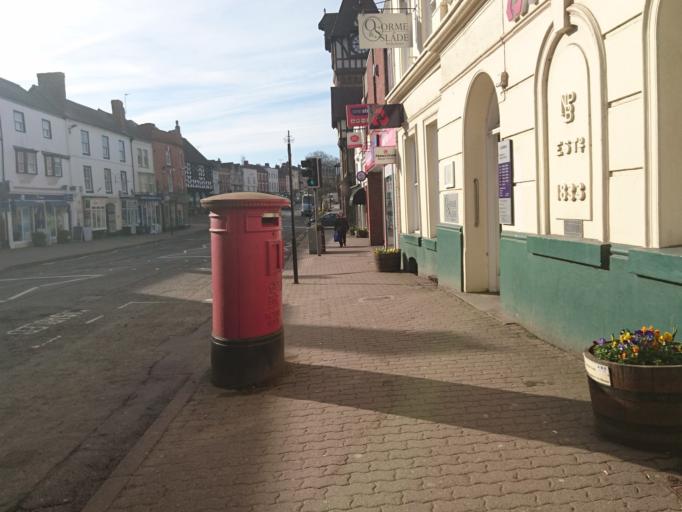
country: GB
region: England
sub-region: Herefordshire
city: Ledbury
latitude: 52.0377
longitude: -2.4236
